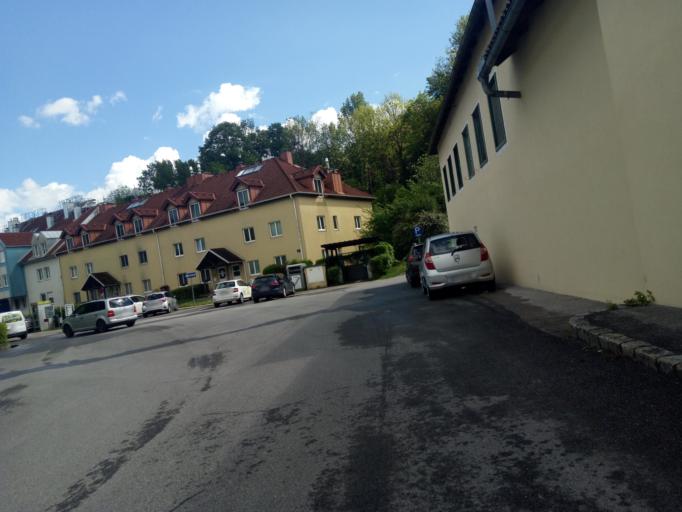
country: AT
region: Lower Austria
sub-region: Politischer Bezirk Modling
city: Breitenfurt bei Wien
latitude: 48.1407
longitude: 16.1365
